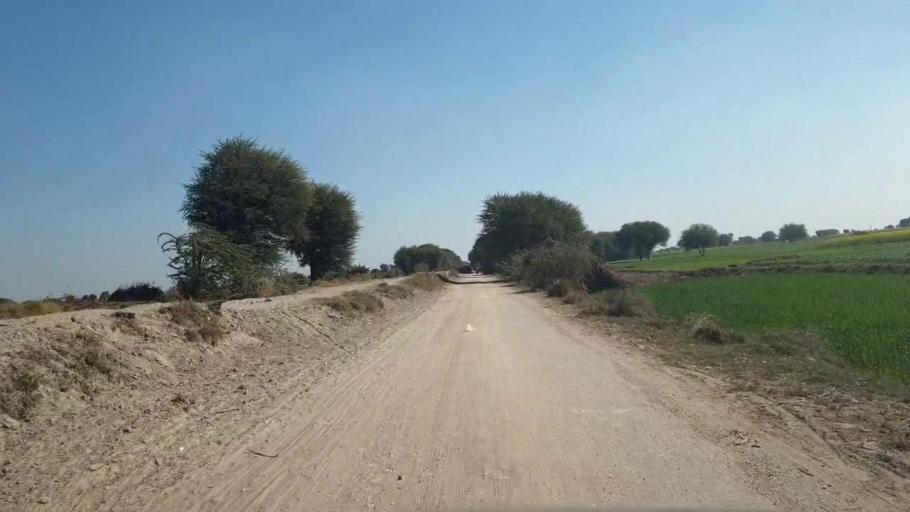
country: PK
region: Sindh
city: Shahpur Chakar
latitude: 26.1424
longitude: 68.6532
